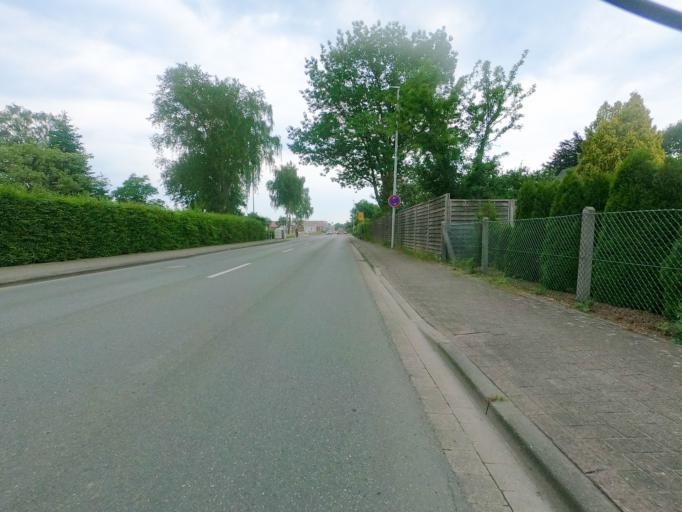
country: DE
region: Lower Saxony
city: Syke
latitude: 52.9781
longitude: 8.8511
